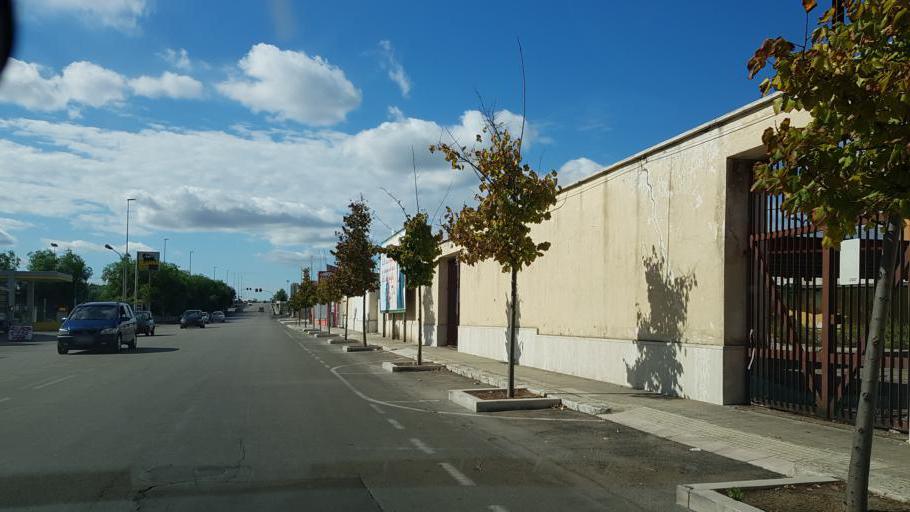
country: IT
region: Apulia
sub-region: Provincia di Lecce
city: Lecce
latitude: 40.3567
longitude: 18.1535
